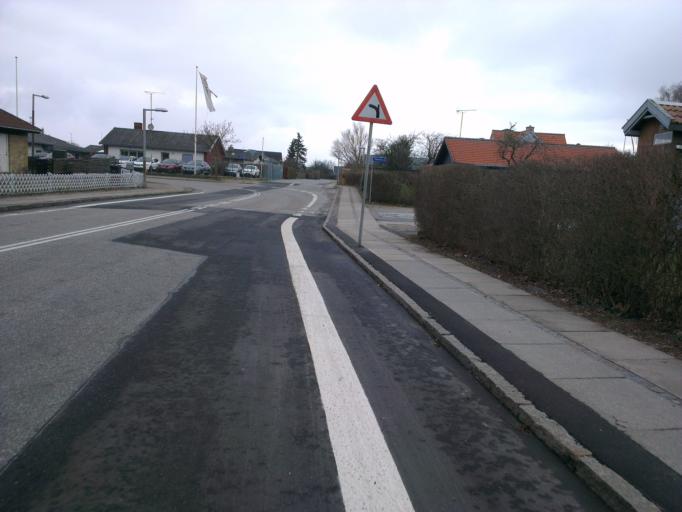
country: DK
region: Capital Region
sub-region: Frederikssund Kommune
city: Frederikssund
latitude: 55.8485
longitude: 12.0615
